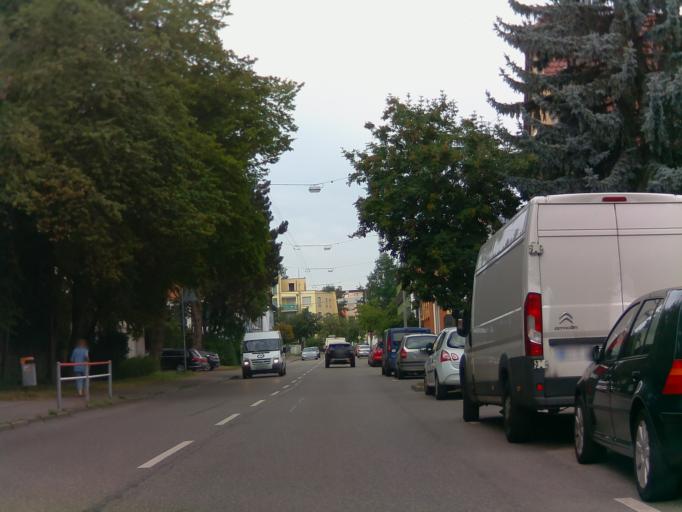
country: DE
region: Baden-Wuerttemberg
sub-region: Regierungsbezirk Stuttgart
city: Leinfelden-Echterdingen
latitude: 48.7277
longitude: 9.1438
